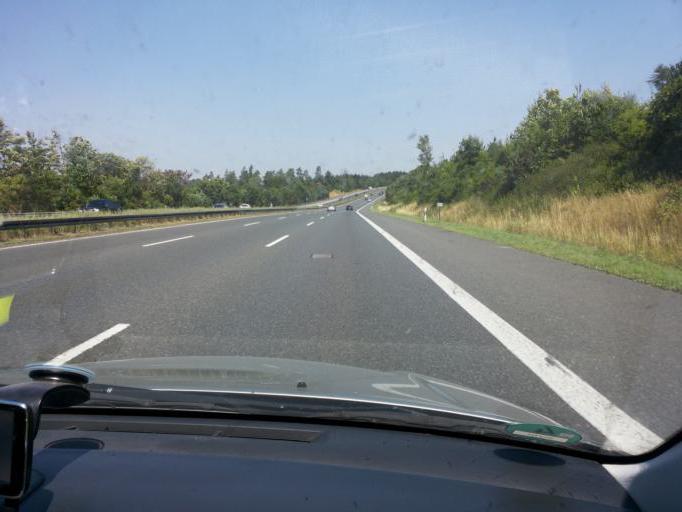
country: DE
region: Bavaria
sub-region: Upper Bavaria
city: Stammham
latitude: 48.8914
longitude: 11.4669
